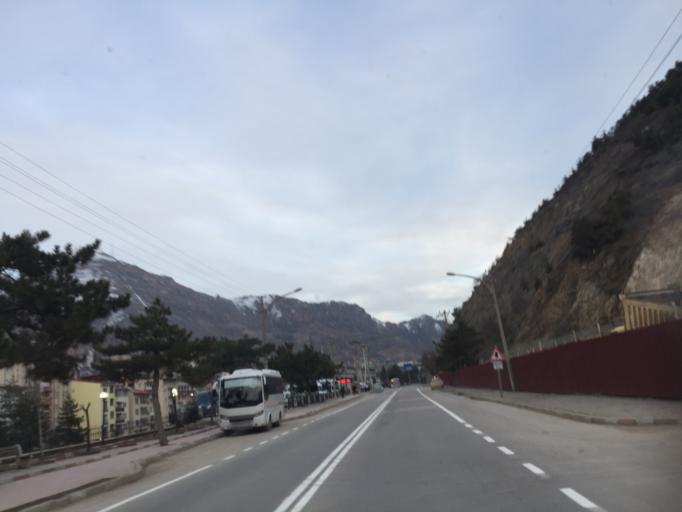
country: TR
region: Gumushane
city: Gumushkhane
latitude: 40.4610
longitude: 39.4705
